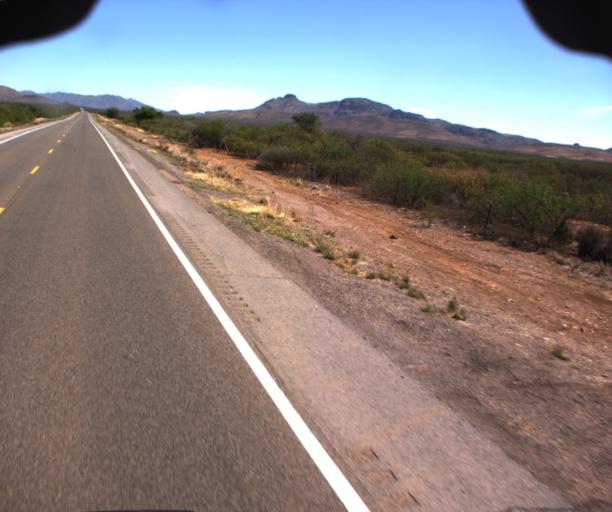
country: US
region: Arizona
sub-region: Cochise County
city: Douglas
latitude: 31.4109
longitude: -109.4973
